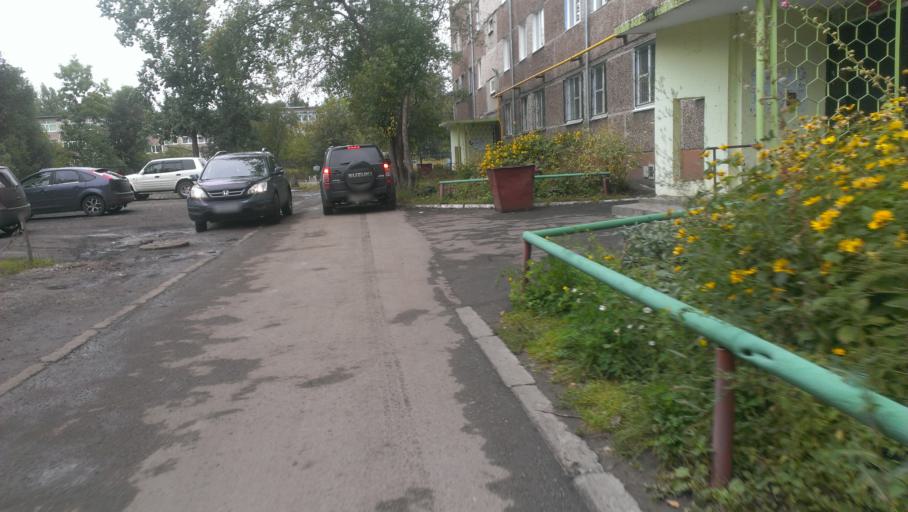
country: RU
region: Altai Krai
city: Novosilikatnyy
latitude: 53.3674
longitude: 83.6817
